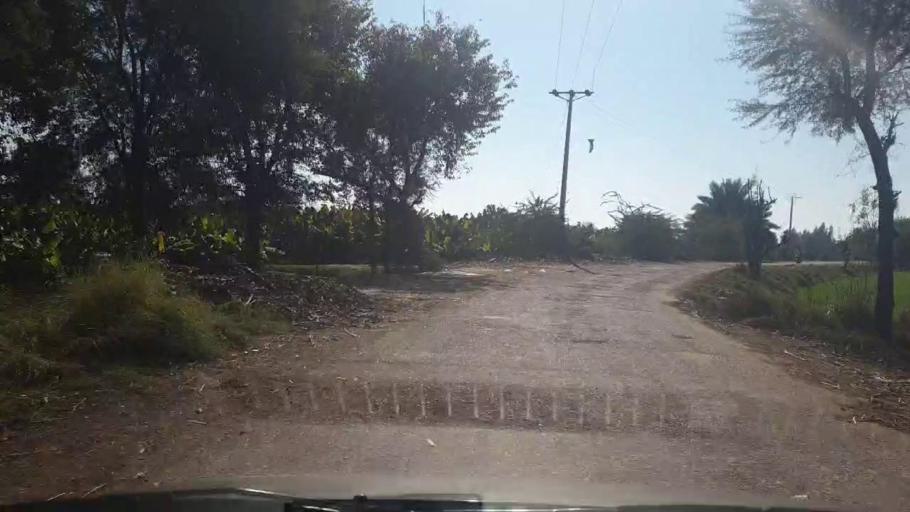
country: PK
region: Sindh
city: Bozdar
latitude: 27.2633
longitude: 68.6533
